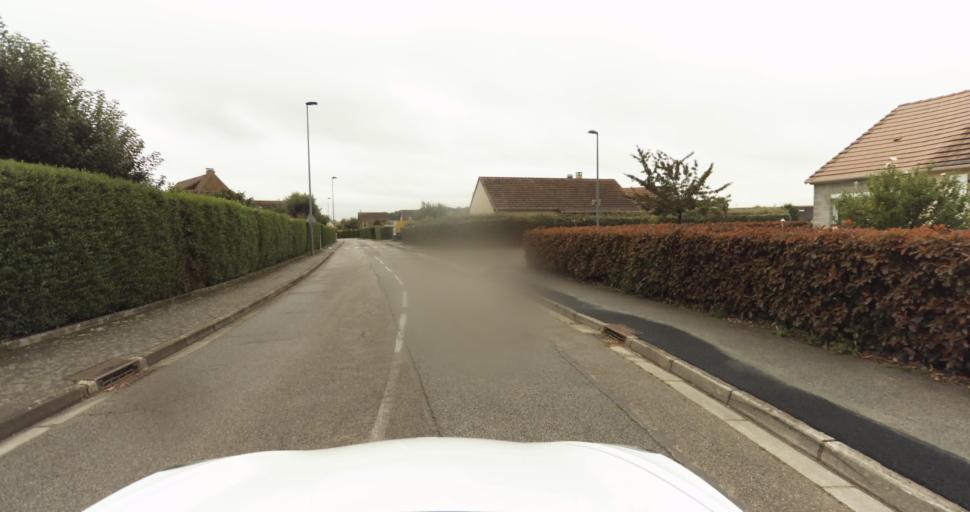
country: FR
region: Haute-Normandie
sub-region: Departement de l'Eure
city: Aviron
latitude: 49.0434
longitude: 1.1379
